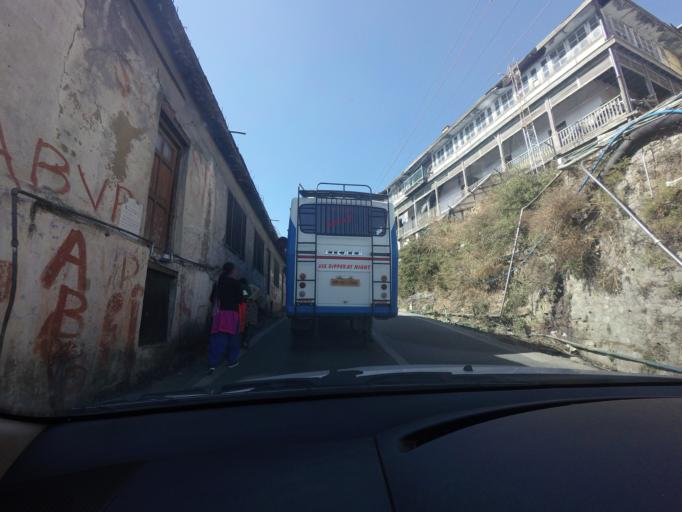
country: IN
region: Himachal Pradesh
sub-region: Shimla
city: Jutogh
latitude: 31.0993
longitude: 77.1407
